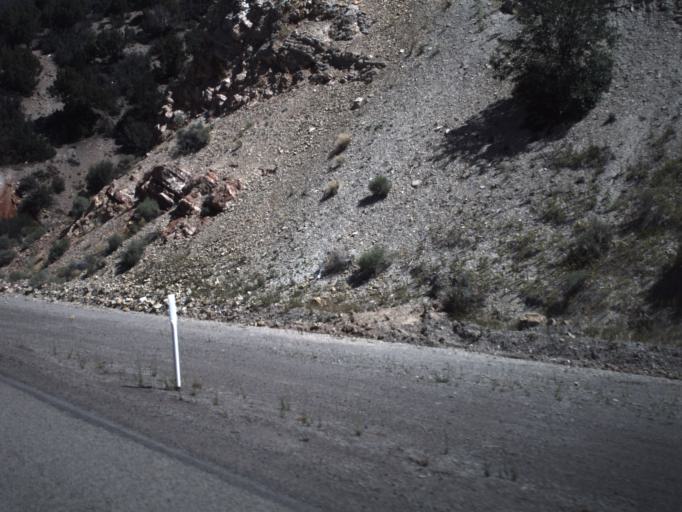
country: US
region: Utah
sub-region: Utah County
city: Mapleton
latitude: 40.0072
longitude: -111.4918
